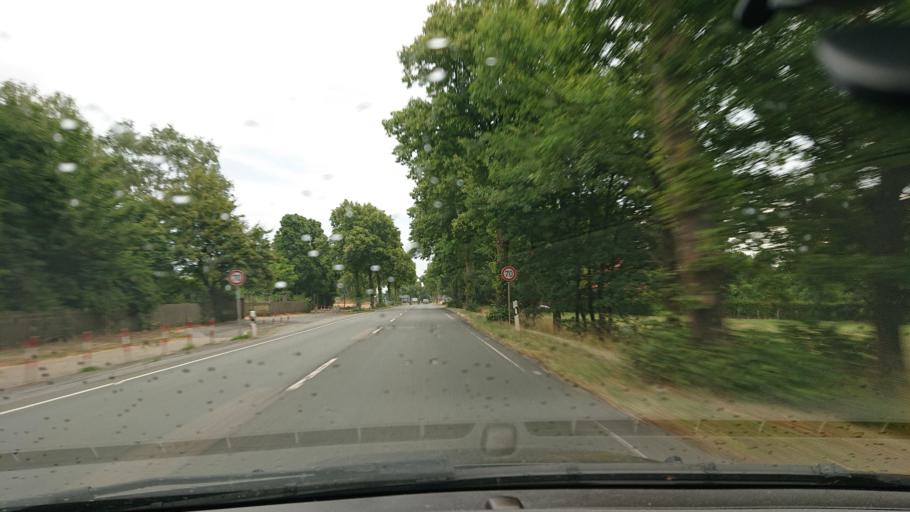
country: DE
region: North Rhine-Westphalia
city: Ahlen
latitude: 51.7075
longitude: 7.9266
